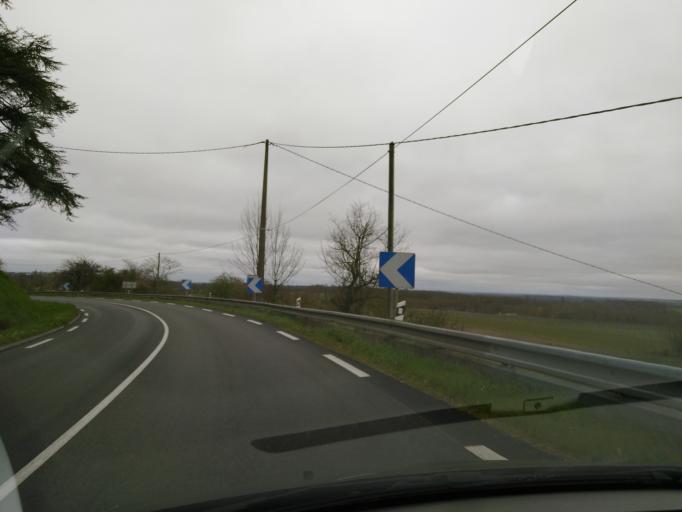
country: FR
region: Aquitaine
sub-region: Departement de la Dordogne
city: Monbazillac
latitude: 44.7414
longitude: 0.5417
